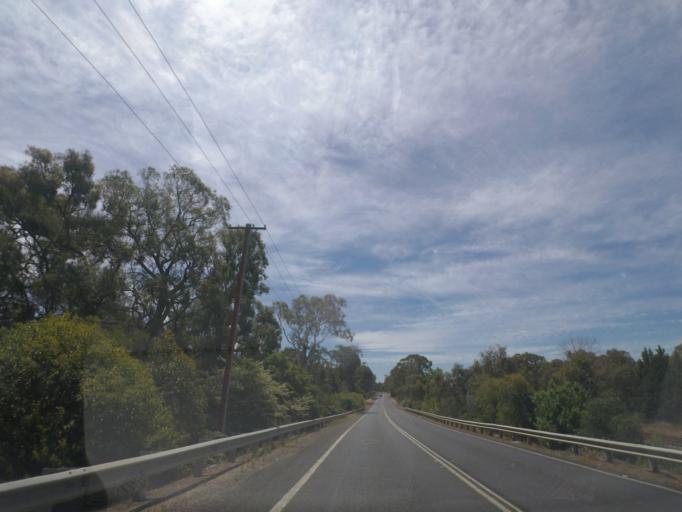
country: AU
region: New South Wales
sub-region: Wollondilly
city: Buxton
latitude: -34.2761
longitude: 150.5763
